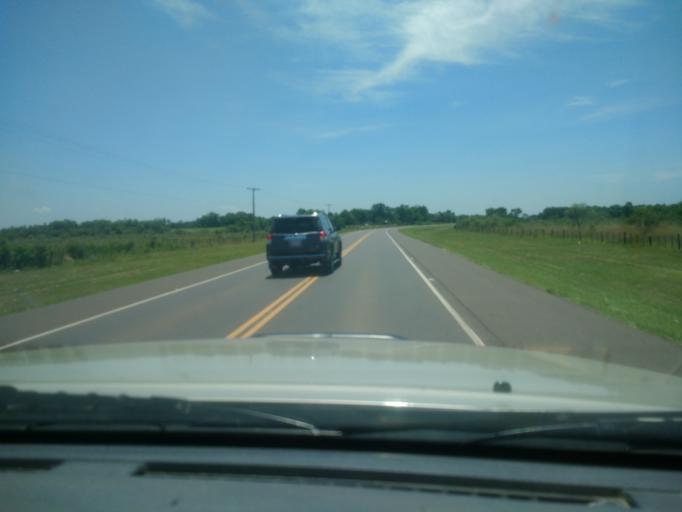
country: PY
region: San Pedro
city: Union
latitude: -24.7170
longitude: -56.5360
